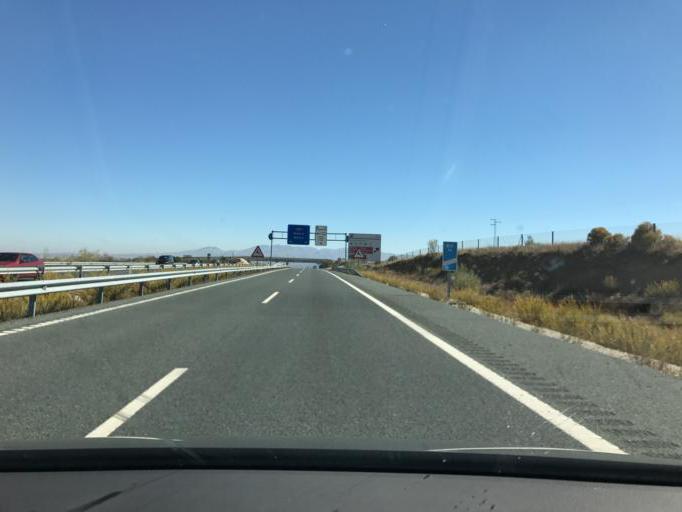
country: ES
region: Andalusia
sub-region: Provincia de Granada
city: Darro
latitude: 37.3212
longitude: -3.2748
